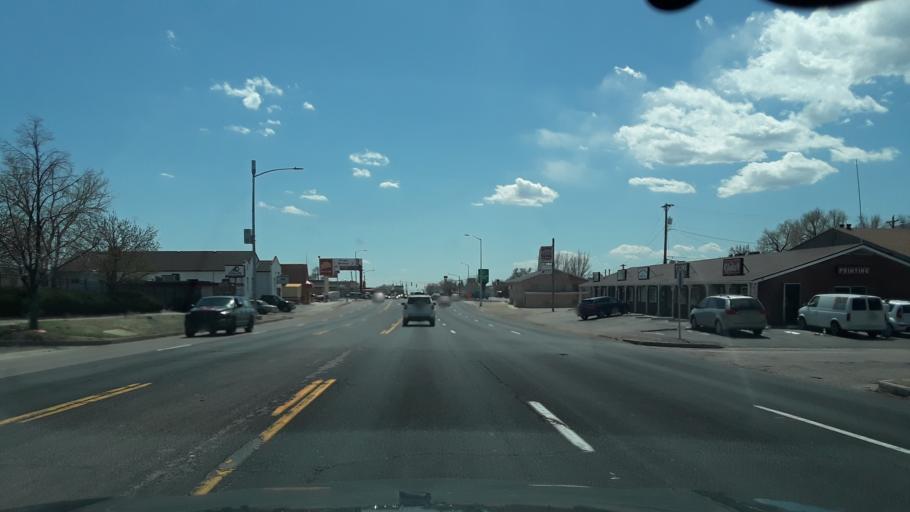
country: US
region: Colorado
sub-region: El Paso County
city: Colorado Springs
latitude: 38.8425
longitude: -104.7759
